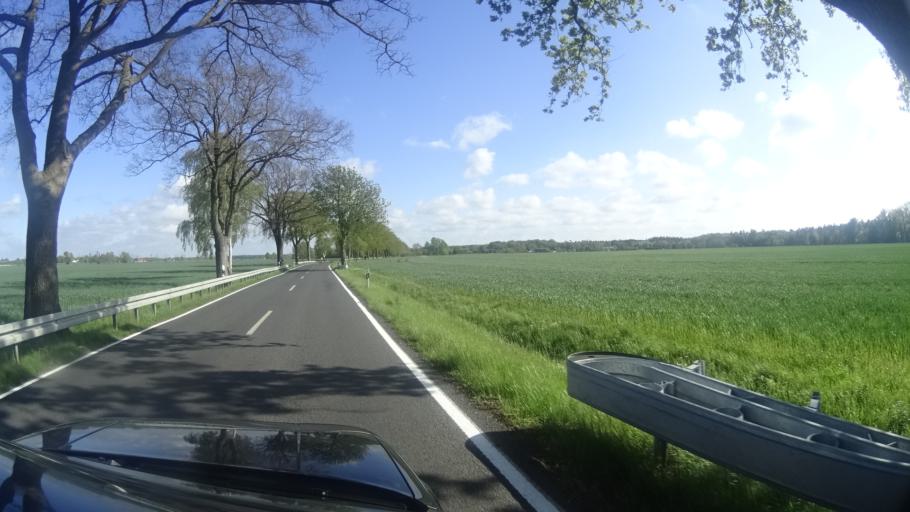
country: DE
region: Mecklenburg-Vorpommern
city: Gelbensande
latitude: 54.2444
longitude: 12.3171
